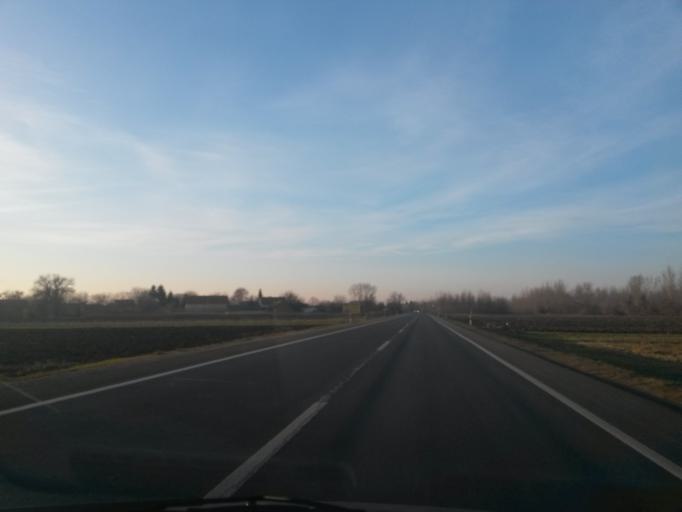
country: HR
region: Varazdinska
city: Jalzabet
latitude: 46.2965
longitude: 16.4889
